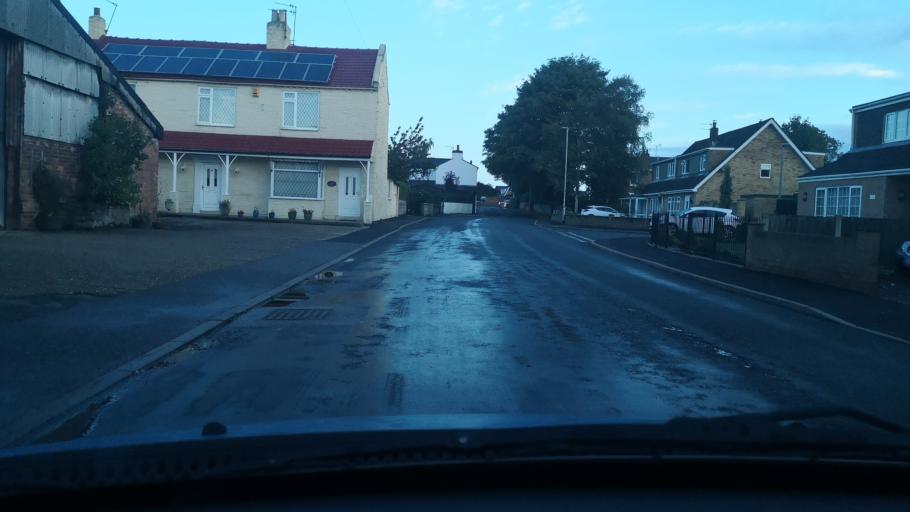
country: GB
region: England
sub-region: East Riding of Yorkshire
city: Skelton
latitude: 53.6910
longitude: -0.8329
